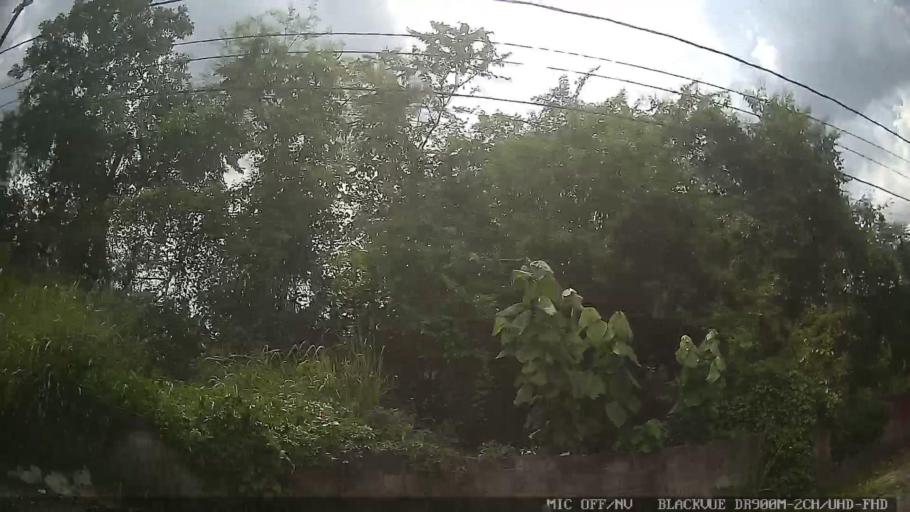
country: BR
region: Sao Paulo
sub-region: Ribeirao Pires
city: Ribeirao Pires
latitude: -23.7178
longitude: -46.4291
